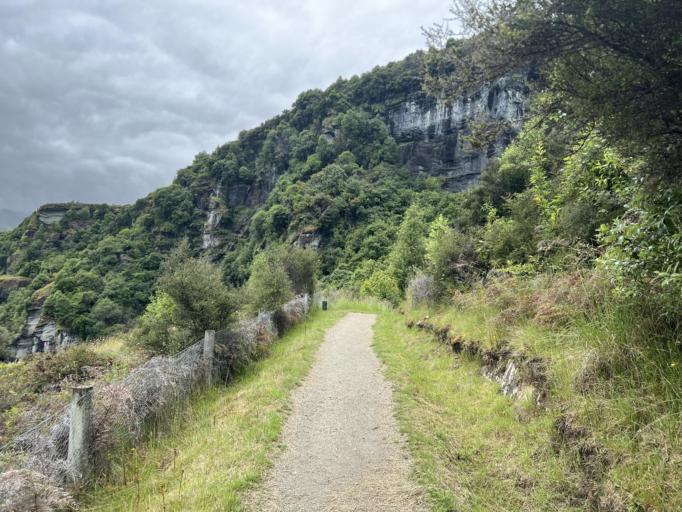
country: NZ
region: Otago
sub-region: Queenstown-Lakes District
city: Wanaka
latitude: -44.6464
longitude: 168.9649
